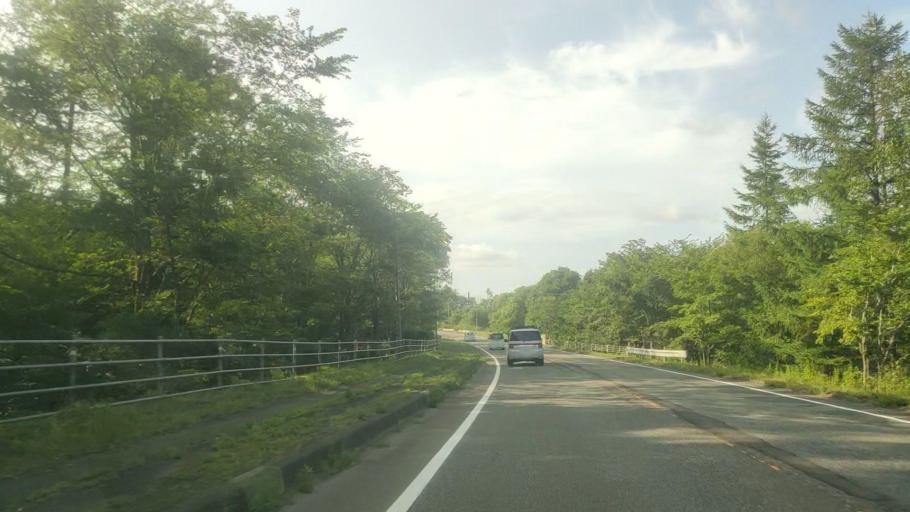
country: JP
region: Hokkaido
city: Chitose
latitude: 42.8730
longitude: 141.8222
